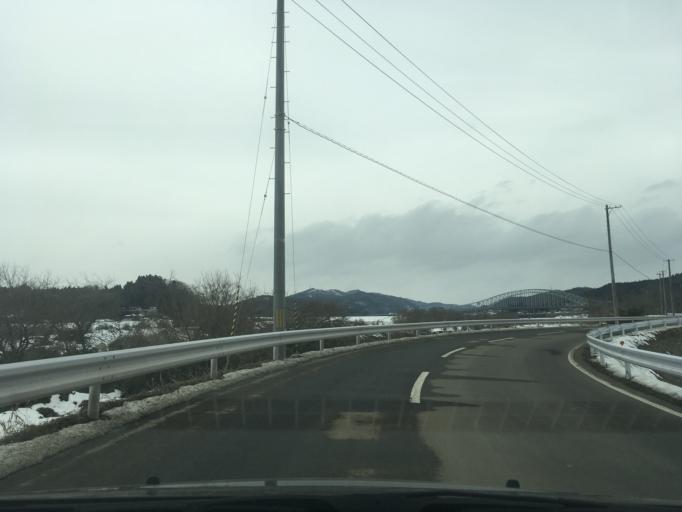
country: JP
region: Iwate
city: Ichinoseki
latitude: 38.8881
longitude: 141.2657
